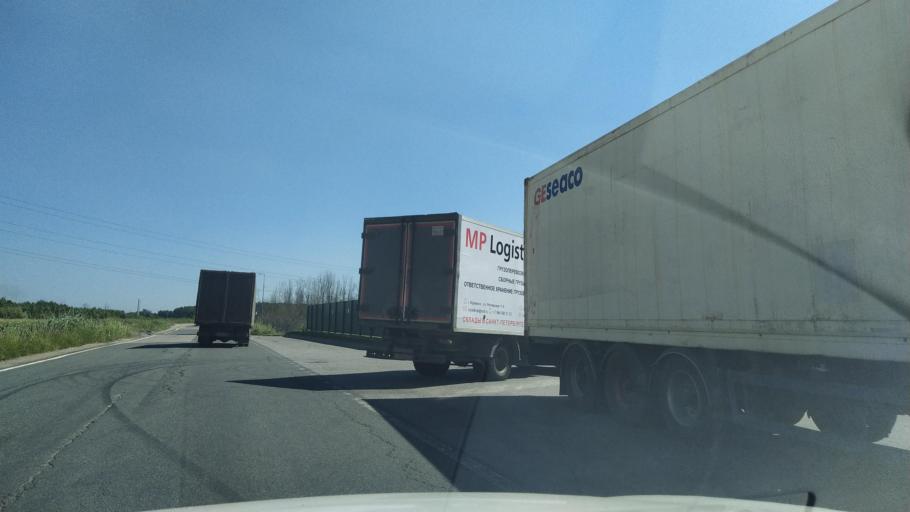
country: RU
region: St.-Petersburg
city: Krasnogvargeisky
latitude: 60.0002
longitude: 30.4526
